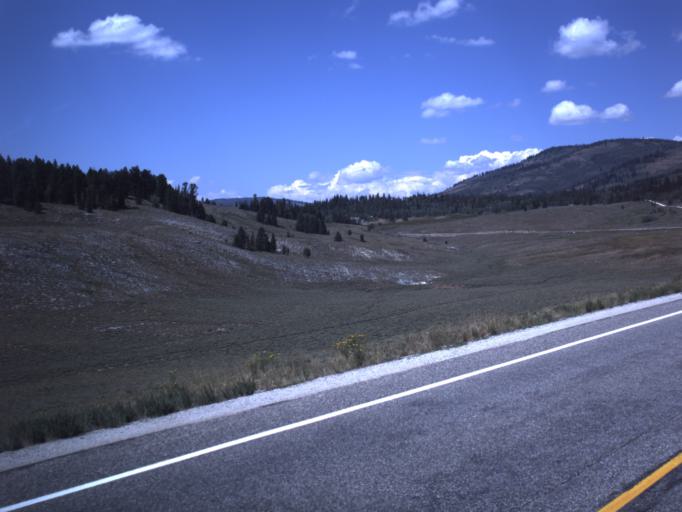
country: US
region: Idaho
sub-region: Bear Lake County
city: Paris
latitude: 41.9436
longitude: -111.4816
